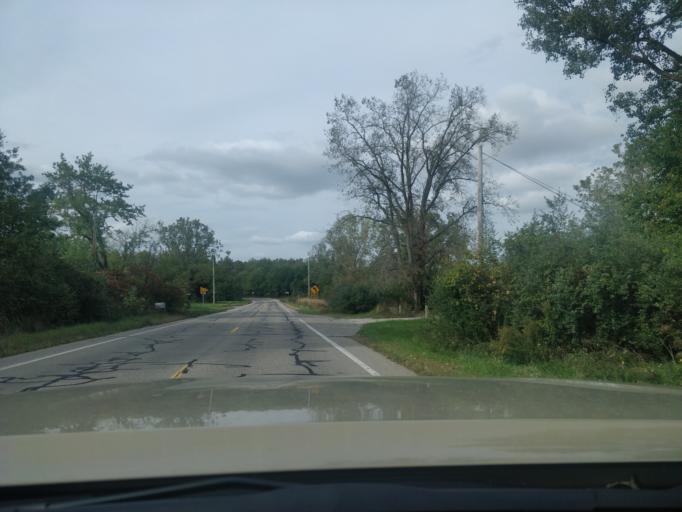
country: US
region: Michigan
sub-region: Wayne County
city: Romulus
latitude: 42.1841
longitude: -83.3708
